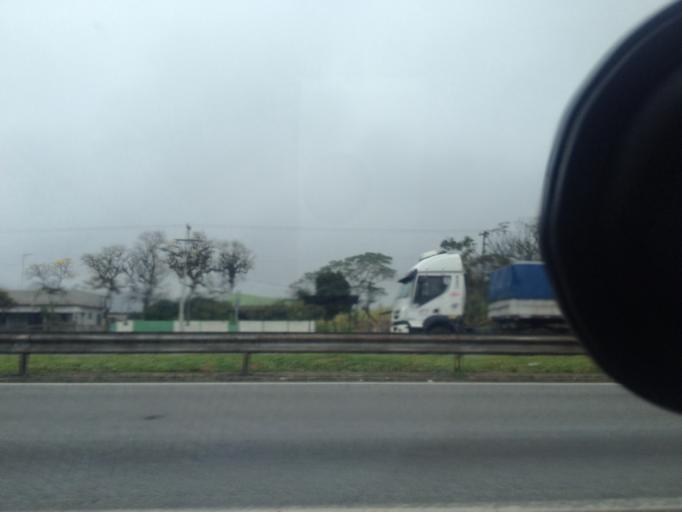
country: BR
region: Rio de Janeiro
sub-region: Porto Real
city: Porto Real
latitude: -22.4523
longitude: -44.3583
